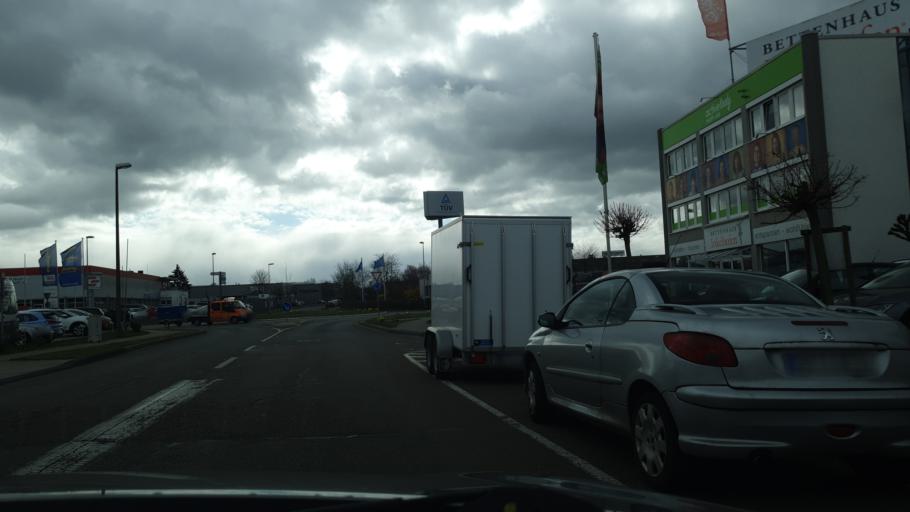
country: DE
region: Rheinland-Pfalz
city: Neuwied
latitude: 50.4359
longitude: 7.4898
